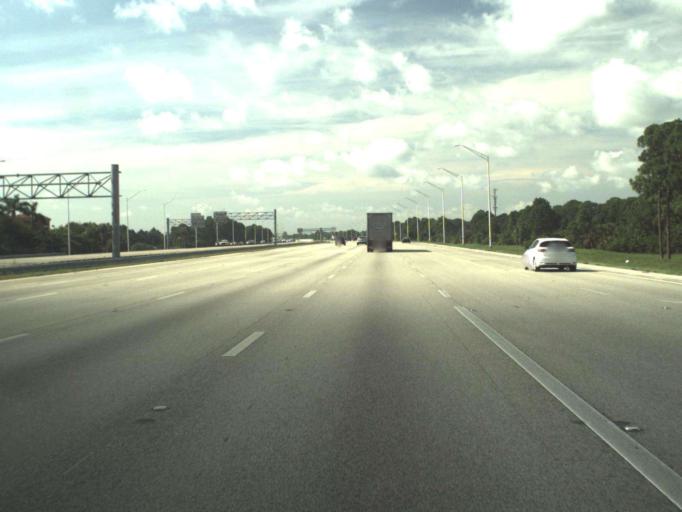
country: US
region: Florida
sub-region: Palm Beach County
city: Limestone Creek
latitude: 26.9261
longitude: -80.1481
